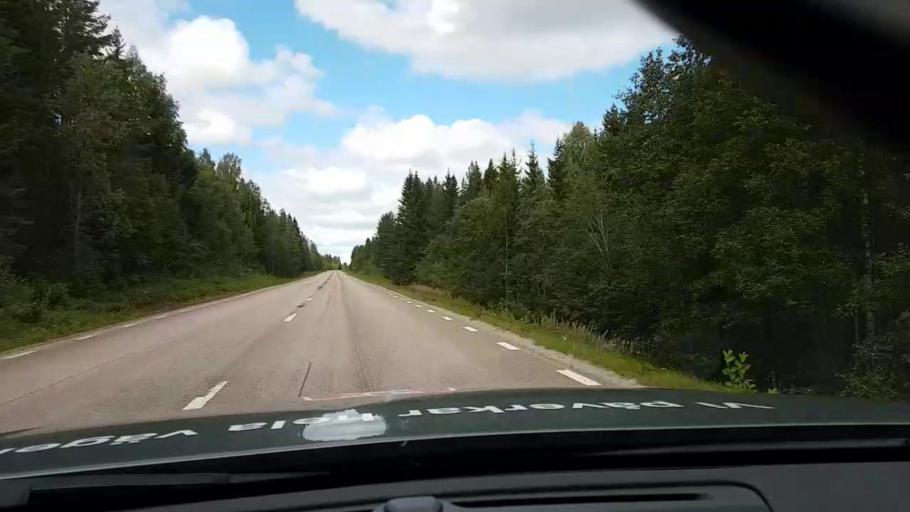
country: SE
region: Vaesternorrland
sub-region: OErnskoeldsviks Kommun
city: Bredbyn
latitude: 63.4679
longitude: 18.1026
